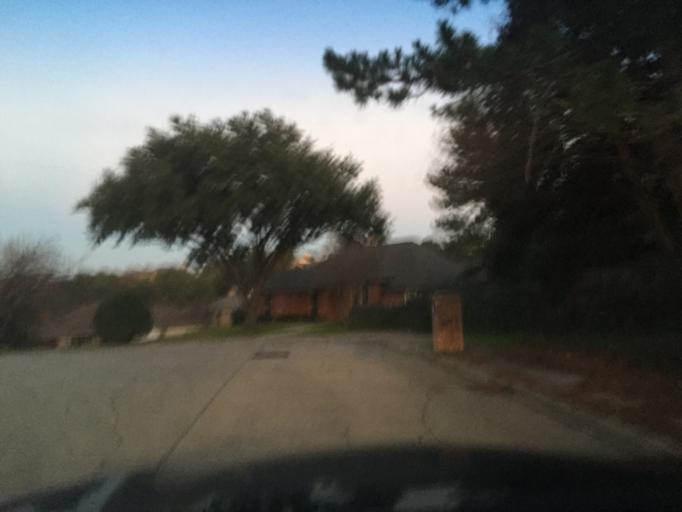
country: US
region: Texas
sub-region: Dallas County
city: Carrollton
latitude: 32.9896
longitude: -96.8975
